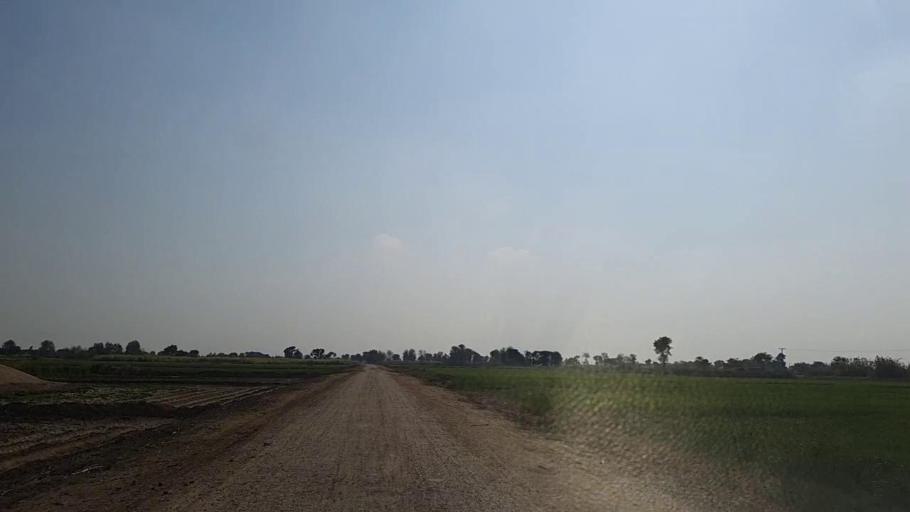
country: PK
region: Sindh
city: Daur
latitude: 26.4415
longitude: 68.2333
